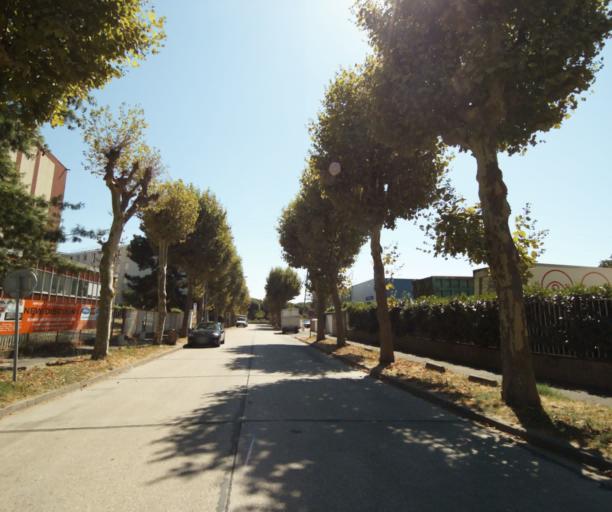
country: FR
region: Ile-de-France
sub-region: Departement des Hauts-de-Seine
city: Villeneuve-la-Garenne
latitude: 48.9443
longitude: 2.3188
